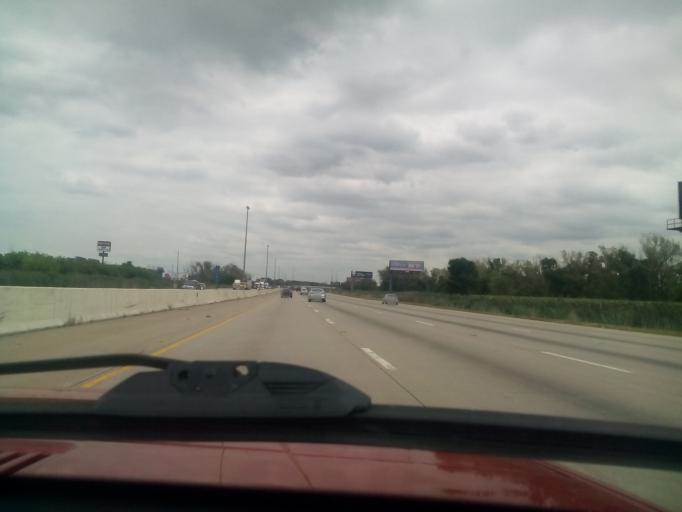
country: US
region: Indiana
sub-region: Lake County
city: Gary
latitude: 41.5697
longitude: -87.3722
